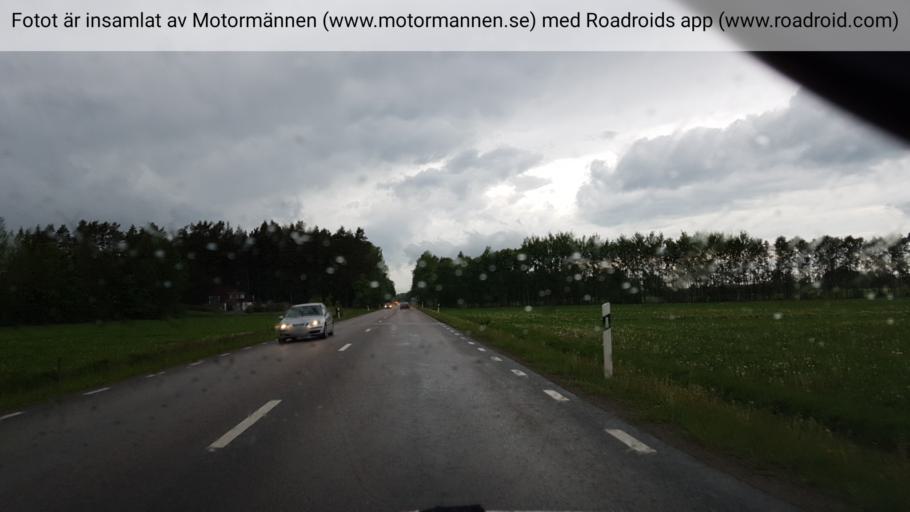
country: SE
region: Vaestra Goetaland
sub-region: Tidaholms Kommun
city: Olofstorp
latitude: 58.3567
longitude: 14.0431
